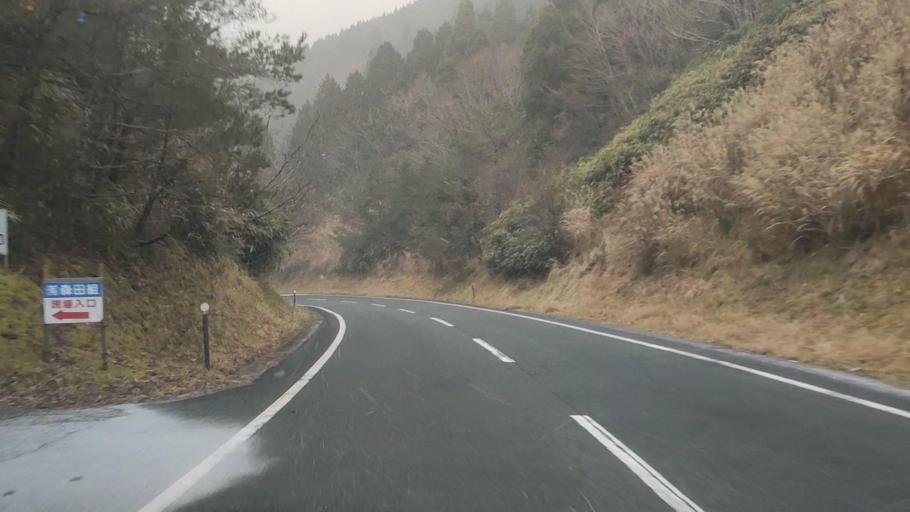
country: JP
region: Kumamoto
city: Matsubase
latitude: 32.5677
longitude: 130.9095
